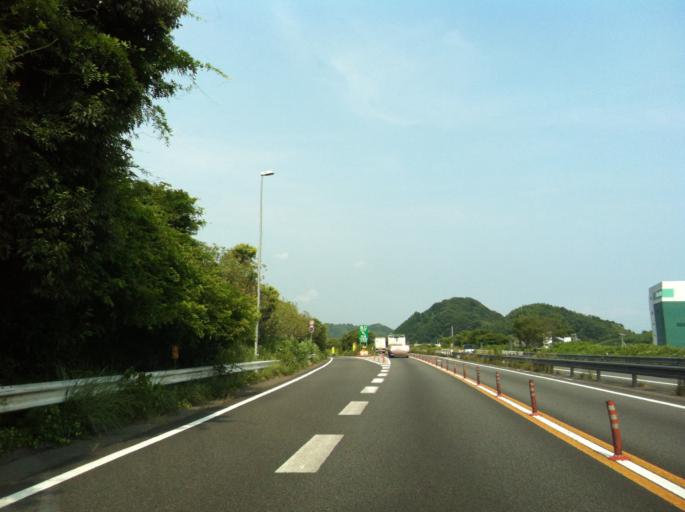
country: JP
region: Shizuoka
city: Fujieda
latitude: 34.8692
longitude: 138.2218
